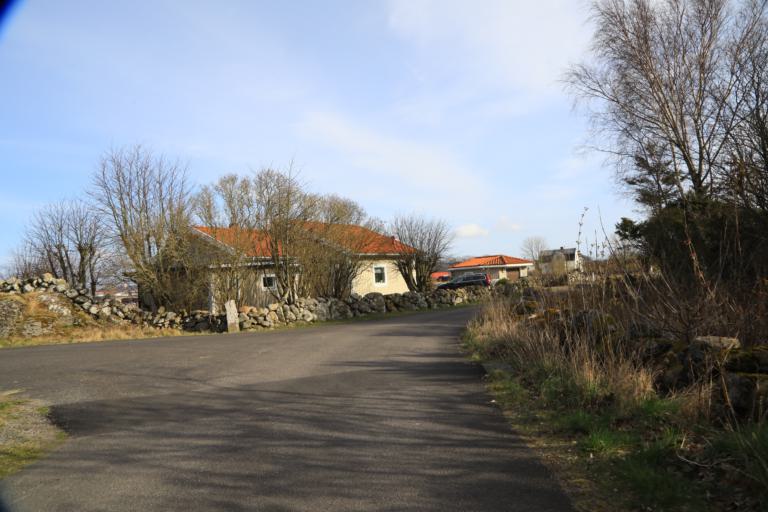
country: SE
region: Halland
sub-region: Varbergs Kommun
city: Varberg
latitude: 57.1230
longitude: 12.2197
